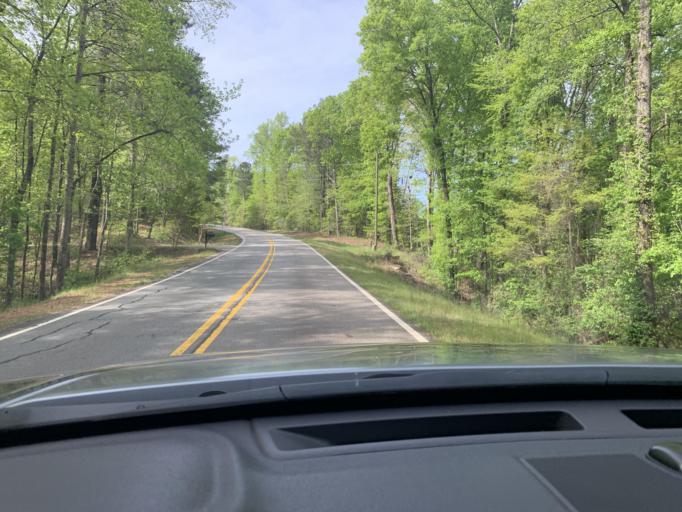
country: US
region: Georgia
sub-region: Oconee County
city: Watkinsville
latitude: 33.8334
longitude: -83.5055
